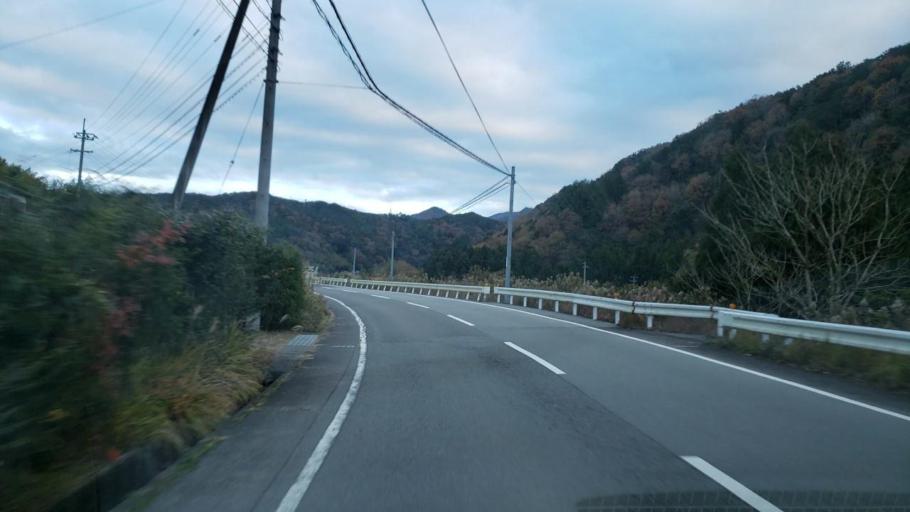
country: JP
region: Tokushima
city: Wakimachi
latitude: 34.1808
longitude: 134.2377
